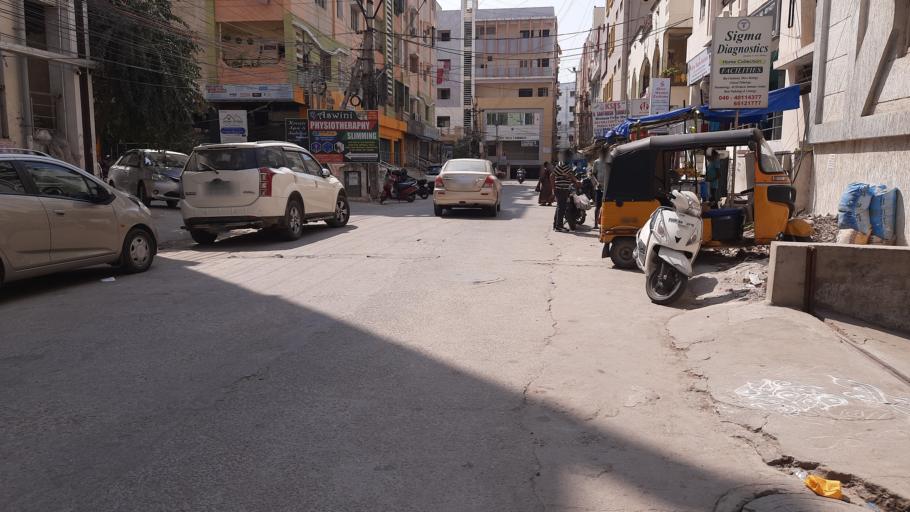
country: IN
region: Telangana
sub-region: Rangareddi
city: Kukatpalli
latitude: 17.5159
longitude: 78.3818
